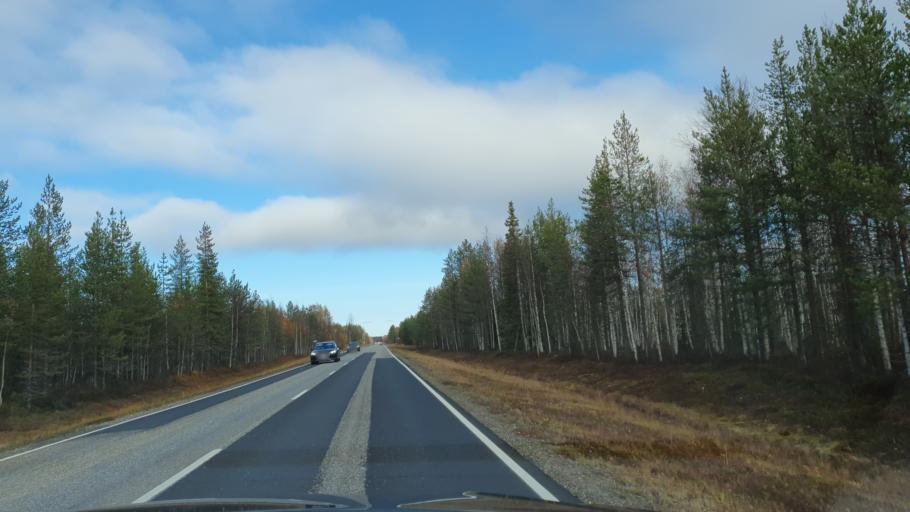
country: FI
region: Lapland
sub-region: Tunturi-Lappi
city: Kittilae
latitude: 67.1967
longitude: 24.9352
